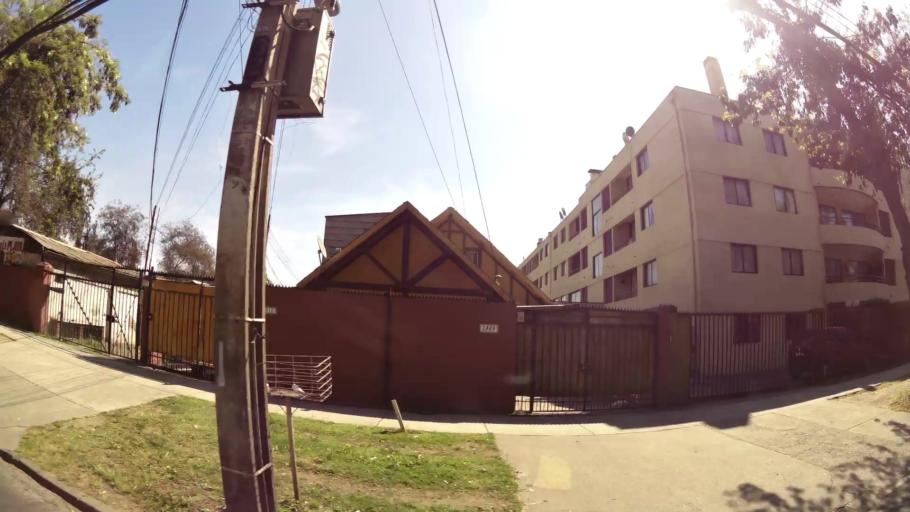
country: CL
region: Santiago Metropolitan
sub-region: Provincia de Santiago
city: Villa Presidente Frei, Nunoa, Santiago, Chile
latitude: -33.4821
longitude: -70.5842
